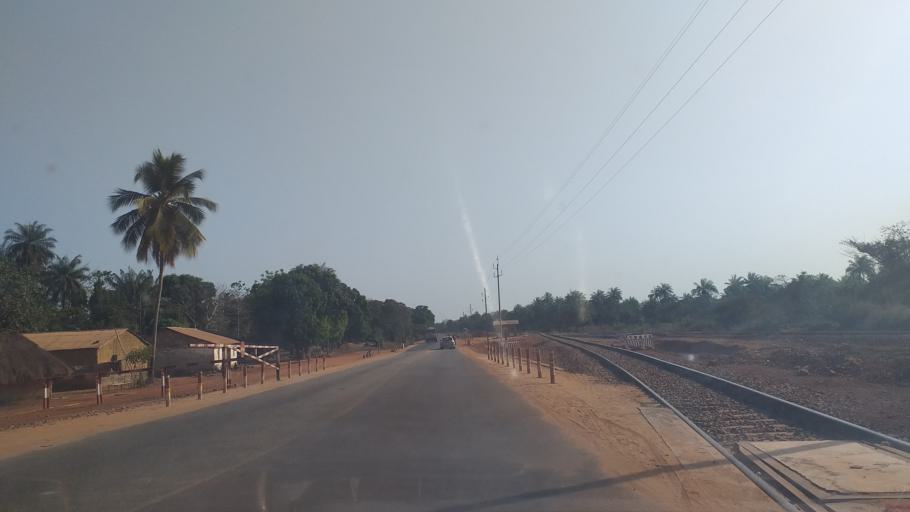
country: GN
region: Boke
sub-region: Boke Prefecture
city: Kamsar
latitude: 10.7387
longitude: -14.5146
